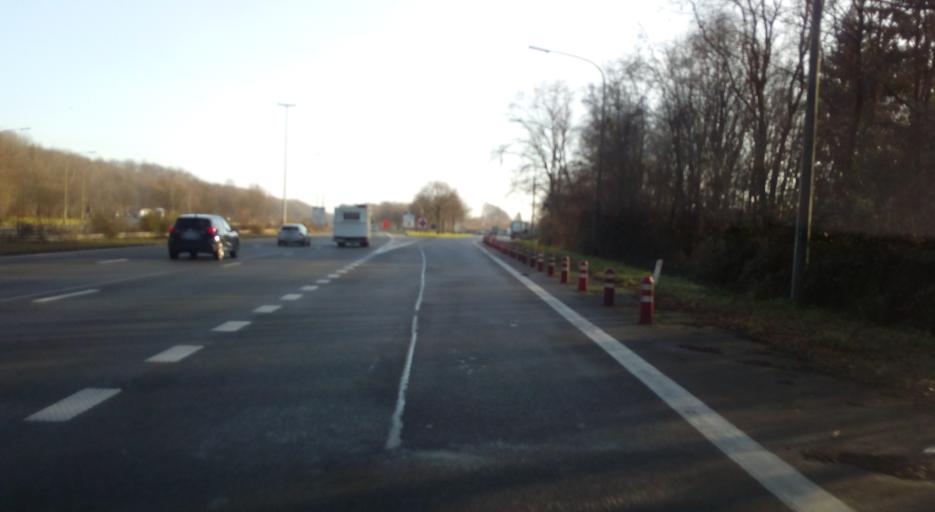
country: BE
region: Wallonia
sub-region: Province du Brabant Wallon
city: Braine-le-Chateau
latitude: 50.6991
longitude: 4.2797
